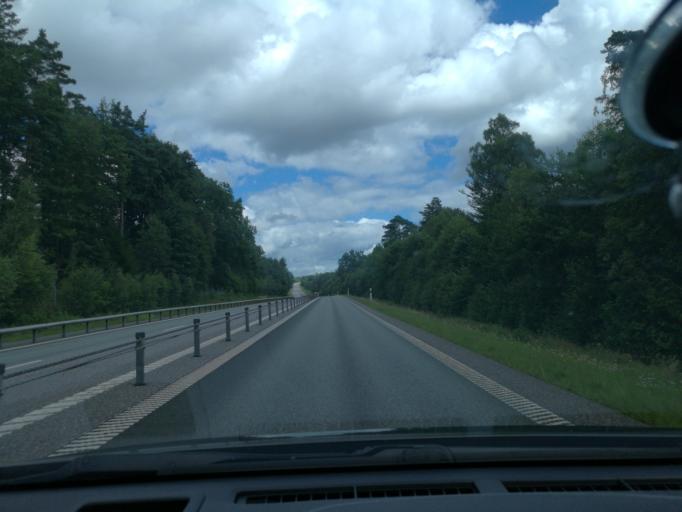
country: SE
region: Skane
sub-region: Hassleholms Kommun
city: Hastveda
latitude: 56.2337
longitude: 13.8959
